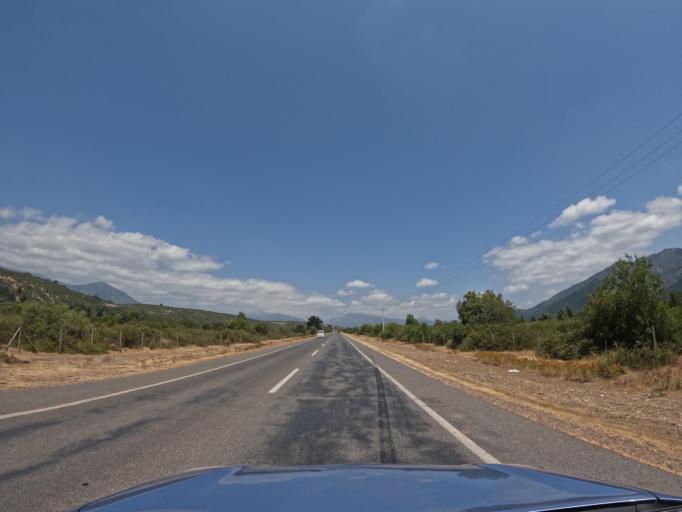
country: CL
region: Maule
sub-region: Provincia de Curico
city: Molina
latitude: -35.1702
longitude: -71.1276
